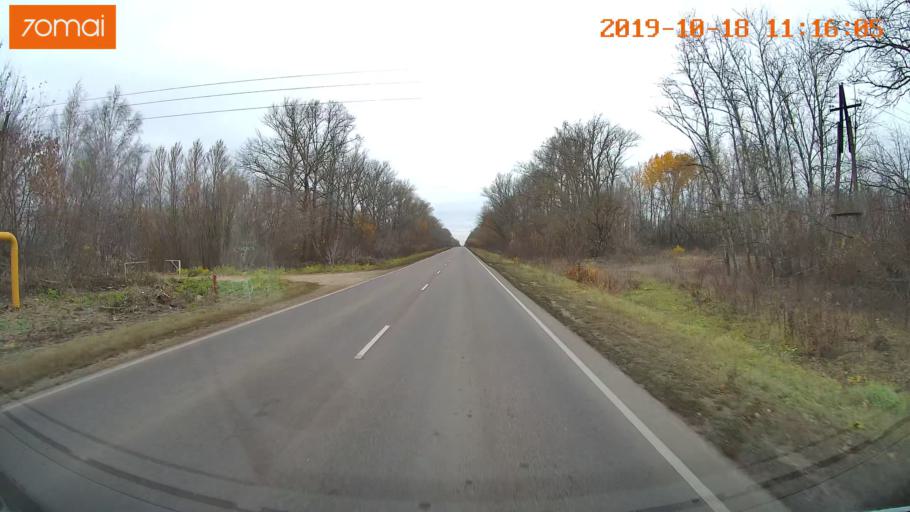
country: RU
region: Tula
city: Kimovsk
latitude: 54.0022
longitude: 38.5482
